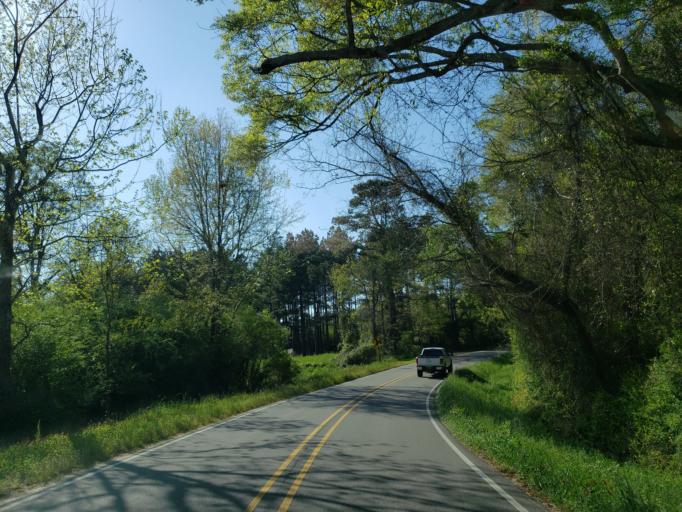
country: US
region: Mississippi
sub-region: Covington County
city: Collins
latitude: 31.6128
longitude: -89.3873
